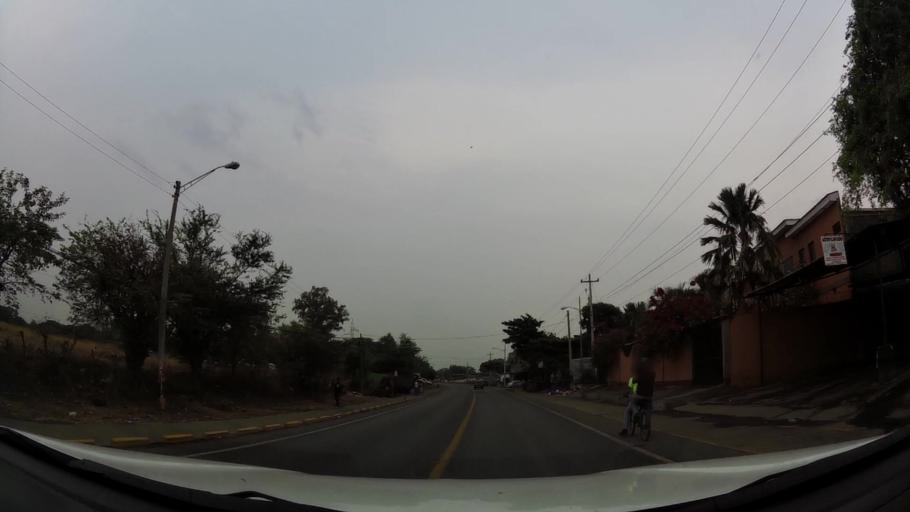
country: NI
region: Leon
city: Leon
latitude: 12.4534
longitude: -86.8644
